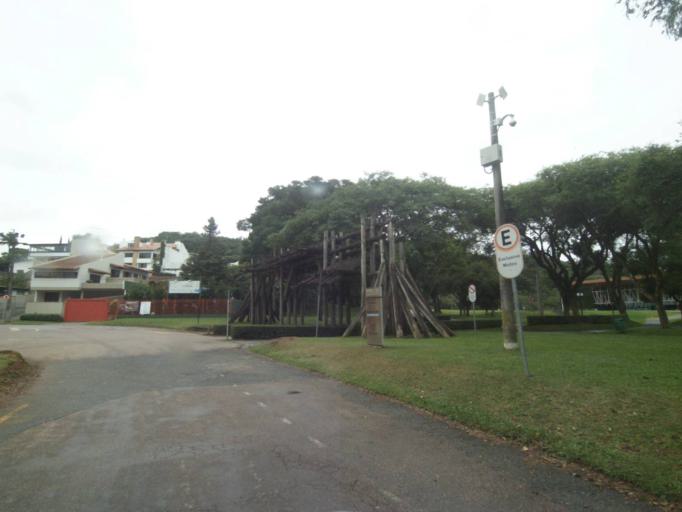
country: BR
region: Parana
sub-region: Curitiba
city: Curitiba
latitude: -25.4292
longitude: -49.3150
